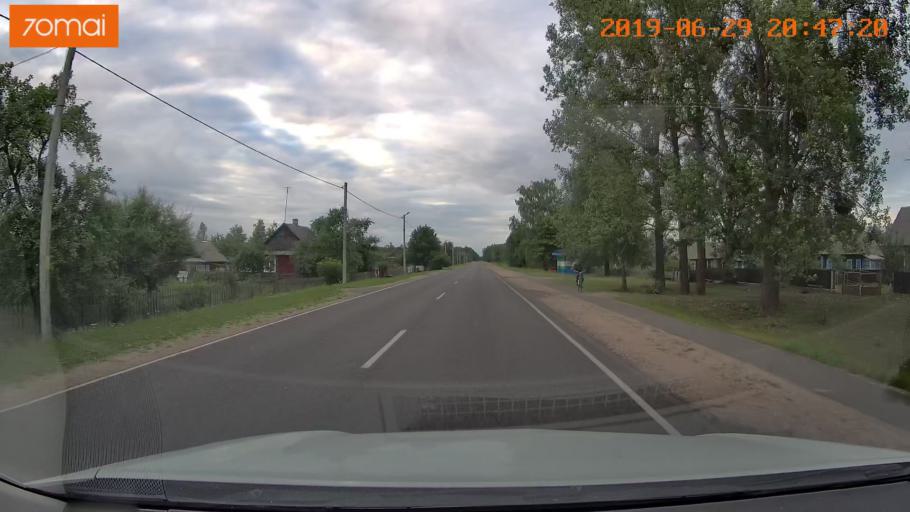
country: BY
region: Brest
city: Hantsavichy
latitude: 52.6374
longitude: 26.3152
